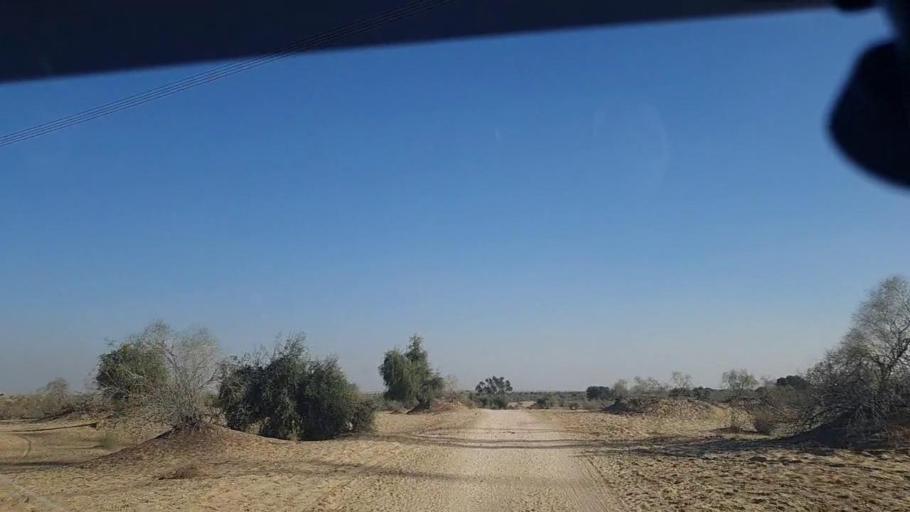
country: PK
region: Sindh
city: Khanpur
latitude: 27.6446
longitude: 69.4053
